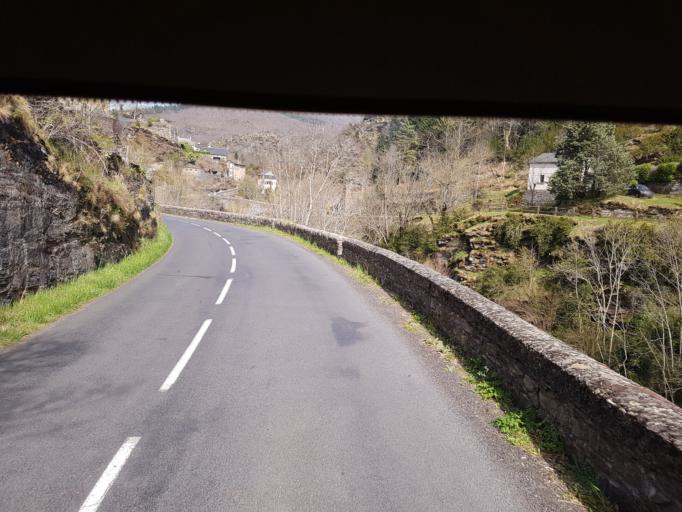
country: FR
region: Languedoc-Roussillon
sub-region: Departement de la Lozere
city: Florac
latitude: 44.2375
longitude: 3.5766
